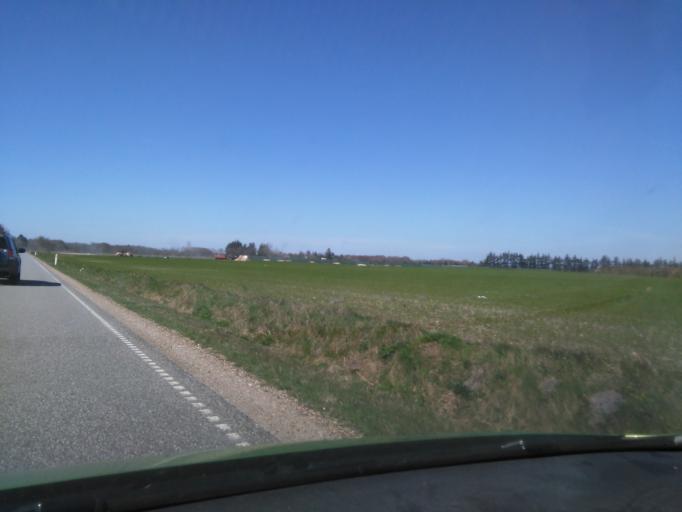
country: DK
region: South Denmark
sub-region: Billund Kommune
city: Grindsted
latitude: 55.6997
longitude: 8.8079
